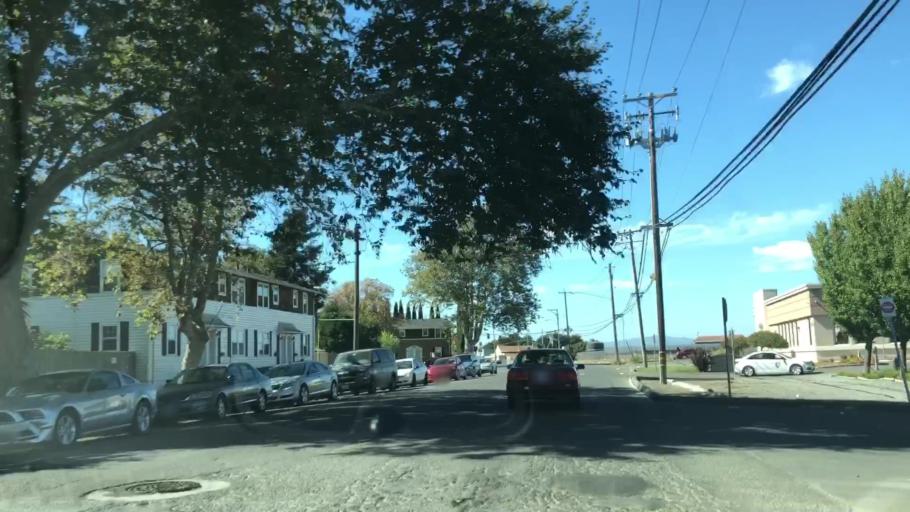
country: US
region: California
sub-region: Solano County
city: Vallejo
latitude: 38.1232
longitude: -122.2632
